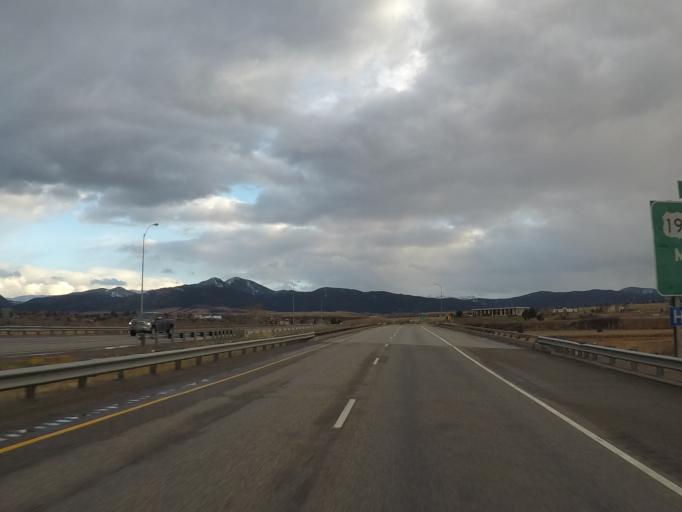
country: US
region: Montana
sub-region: Gallatin County
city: Bozeman
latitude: 45.6804
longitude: -111.0123
